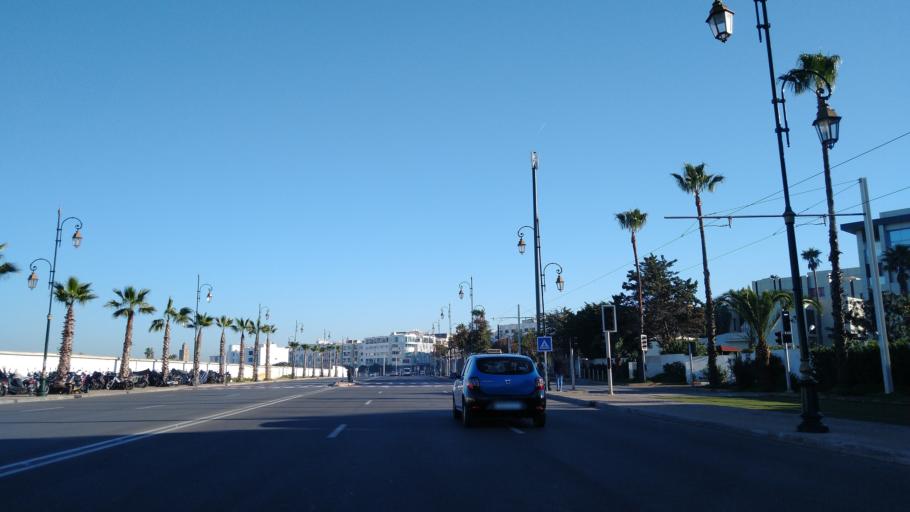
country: MA
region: Rabat-Sale-Zemmour-Zaer
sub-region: Rabat
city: Rabat
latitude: 33.9944
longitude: -6.8532
